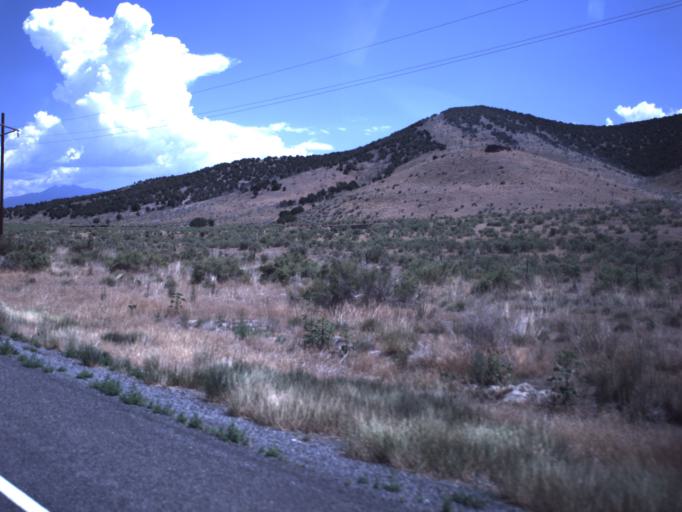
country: US
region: Utah
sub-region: Juab County
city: Nephi
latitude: 39.6118
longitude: -112.1335
